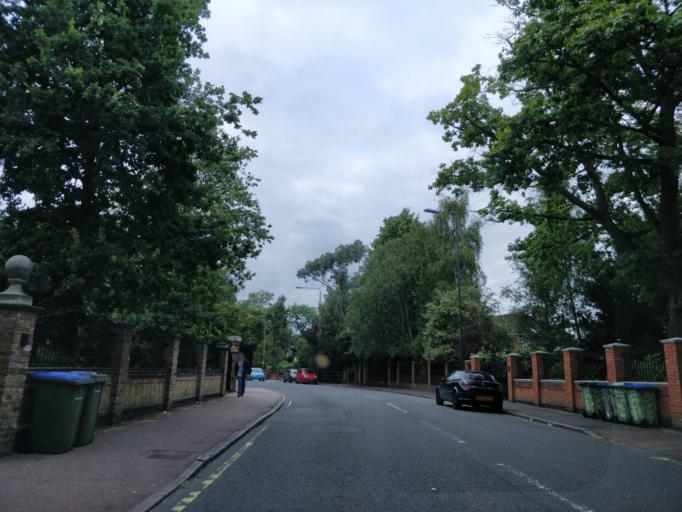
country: GB
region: England
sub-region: Greater London
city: Chislehurst
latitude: 51.4468
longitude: 0.0527
